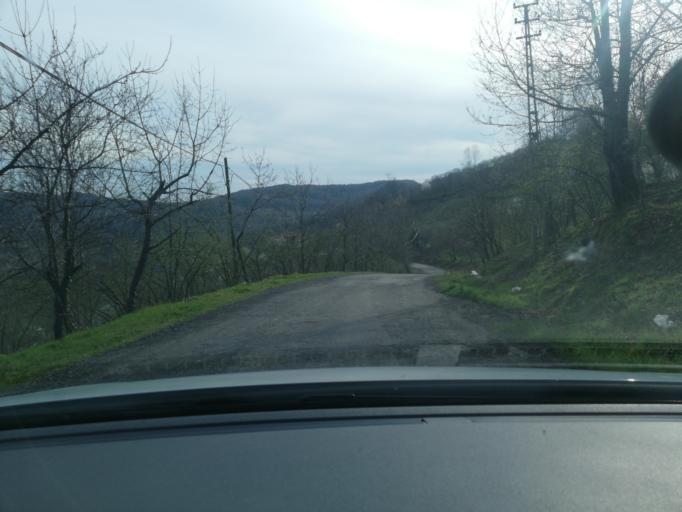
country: TR
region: Zonguldak
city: Kozlu
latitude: 41.3575
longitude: 31.6455
